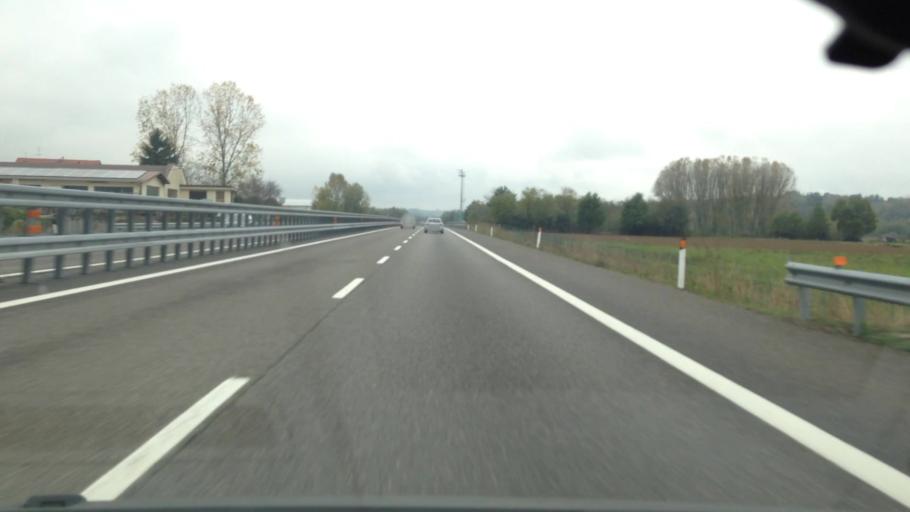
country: IT
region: Piedmont
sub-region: Provincia di Asti
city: Villafranca d'Asti
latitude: 44.9180
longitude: 8.0310
